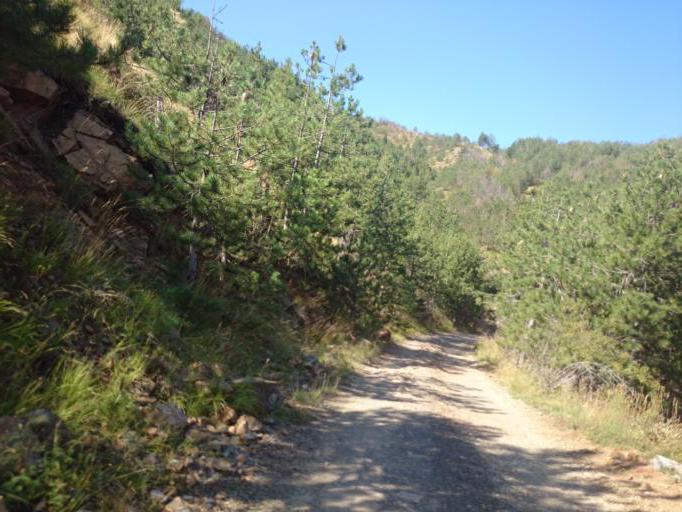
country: AL
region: Diber
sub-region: Rrethi i Bulqizes
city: Martanesh
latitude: 41.4002
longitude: 20.2761
